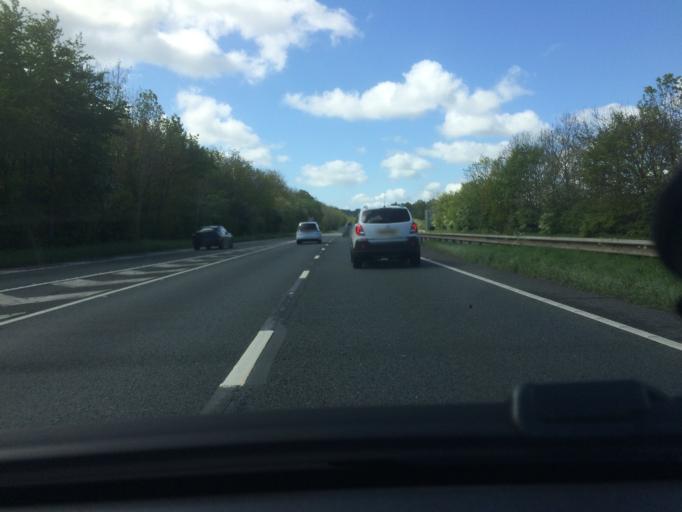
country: GB
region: Wales
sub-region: Wrexham
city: Rossett
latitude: 53.1032
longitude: -2.9593
